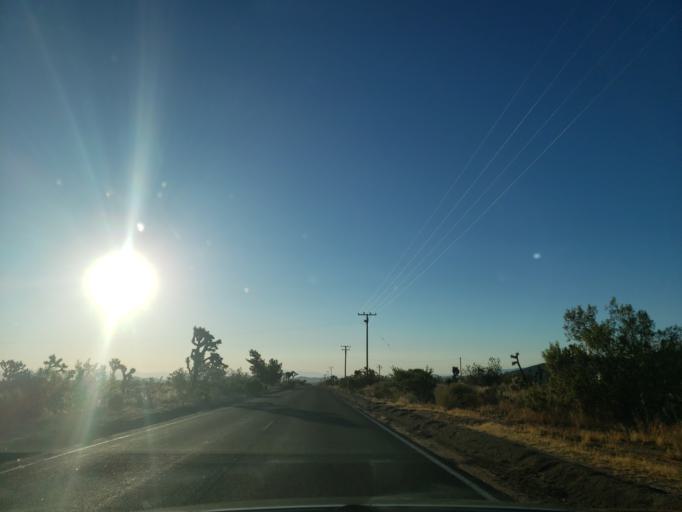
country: US
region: California
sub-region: San Bernardino County
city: Joshua Tree
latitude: 34.1930
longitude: -116.3770
